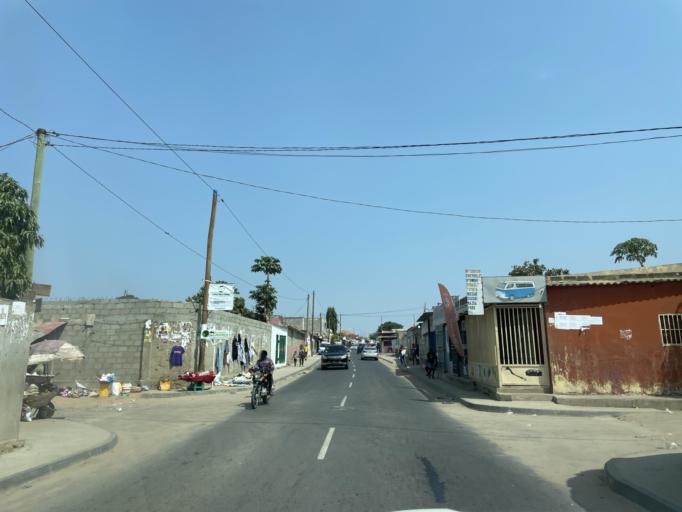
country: AO
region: Luanda
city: Luanda
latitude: -8.9289
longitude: 13.2013
